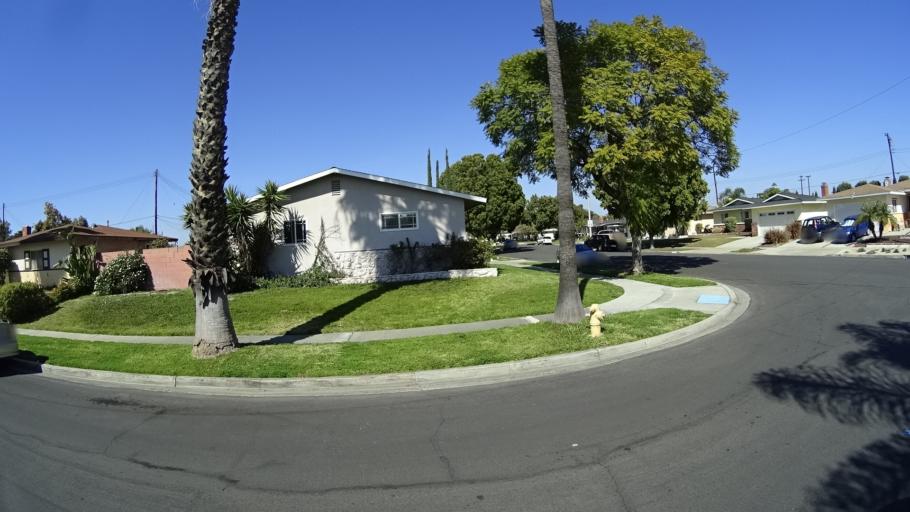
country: US
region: California
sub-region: Orange County
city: Buena Park
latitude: 33.8362
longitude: -117.9868
